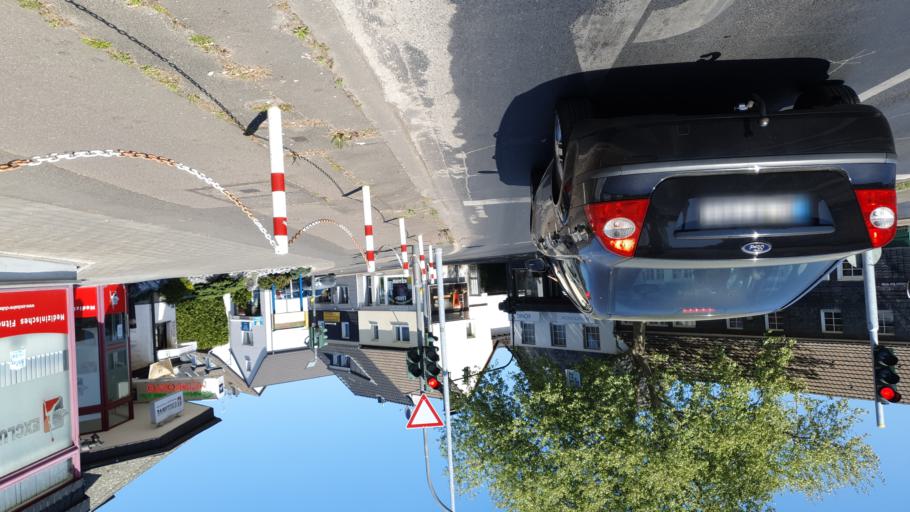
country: DE
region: North Rhine-Westphalia
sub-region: Regierungsbezirk Koln
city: Odenthal
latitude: 51.0138
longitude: 7.0796
